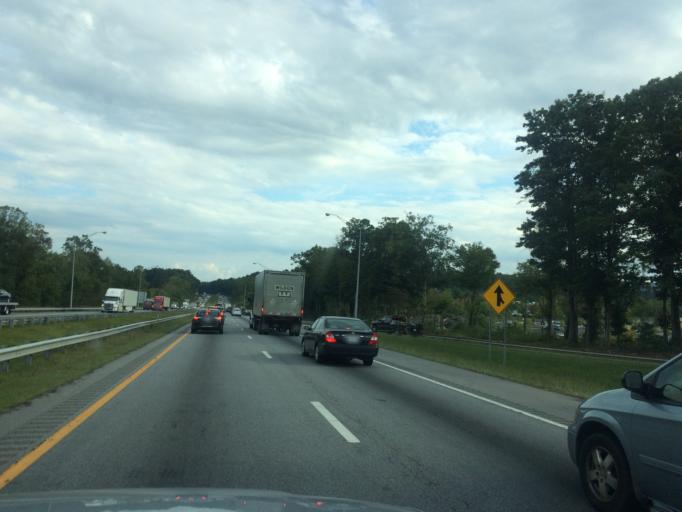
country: US
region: North Carolina
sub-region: Buncombe County
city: Bent Creek
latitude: 35.5320
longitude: -82.6015
